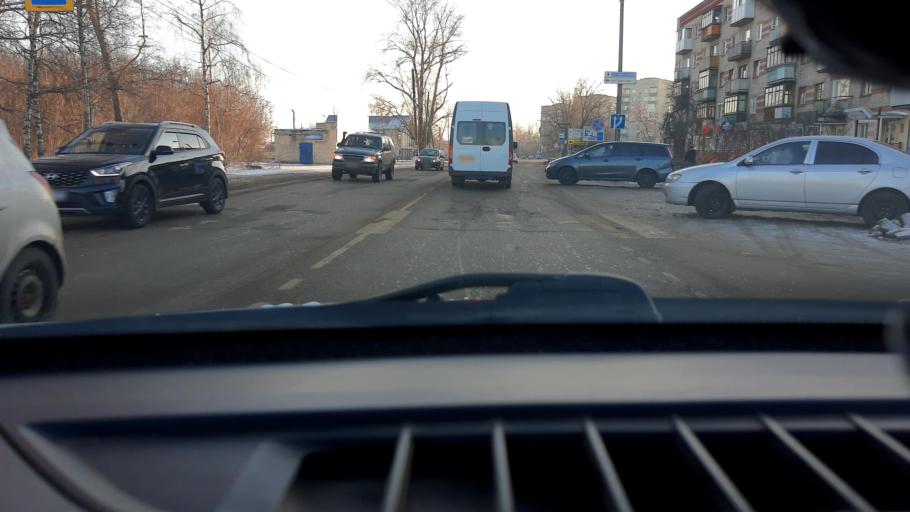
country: RU
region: Nizjnij Novgorod
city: Bor
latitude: 56.3572
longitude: 44.0718
